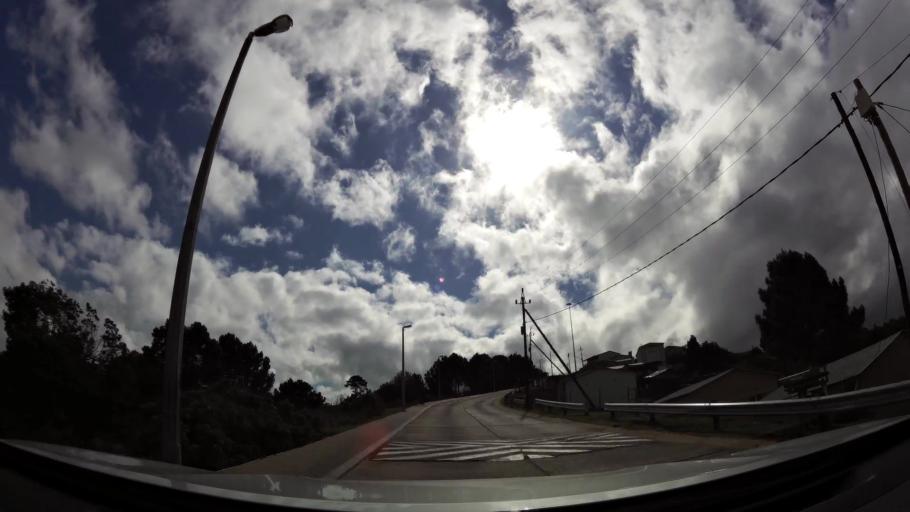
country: ZA
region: Western Cape
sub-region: Eden District Municipality
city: Knysna
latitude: -34.0315
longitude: 23.1000
